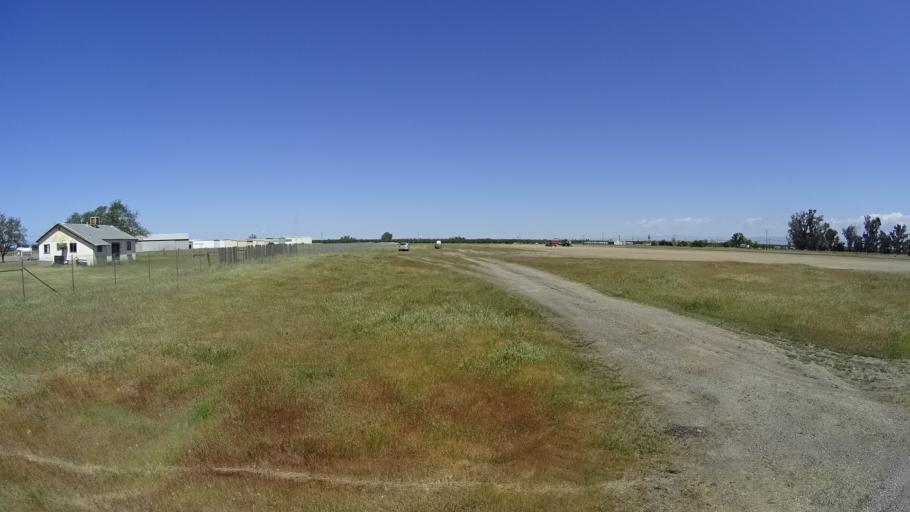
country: US
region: California
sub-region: Glenn County
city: Orland
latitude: 39.7206
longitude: -122.1432
